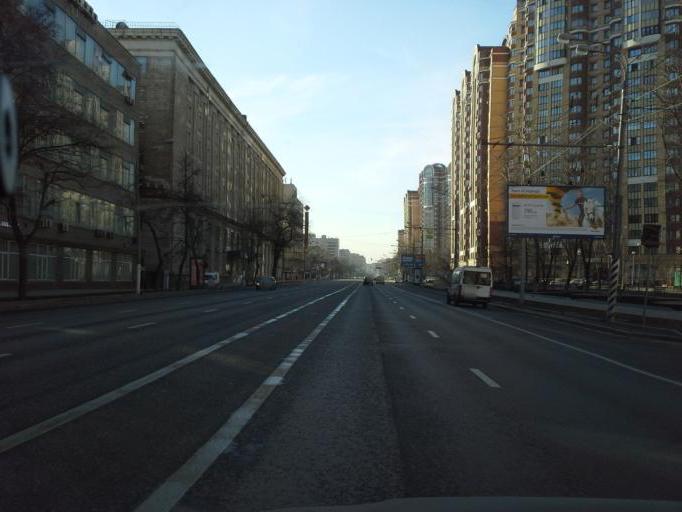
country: RU
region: Moscow
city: Taganskiy
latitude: 55.7371
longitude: 37.6928
